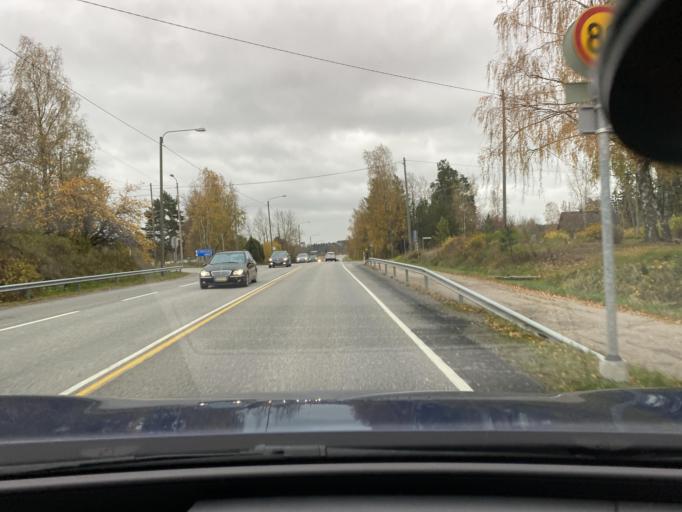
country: FI
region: Varsinais-Suomi
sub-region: Vakka-Suomi
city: Pyhaeranta
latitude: 60.9856
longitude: 21.5873
